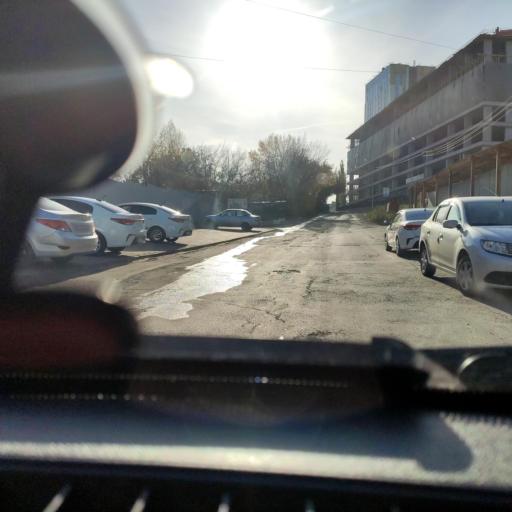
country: RU
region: Bashkortostan
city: Ufa
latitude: 54.7273
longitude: 55.9978
